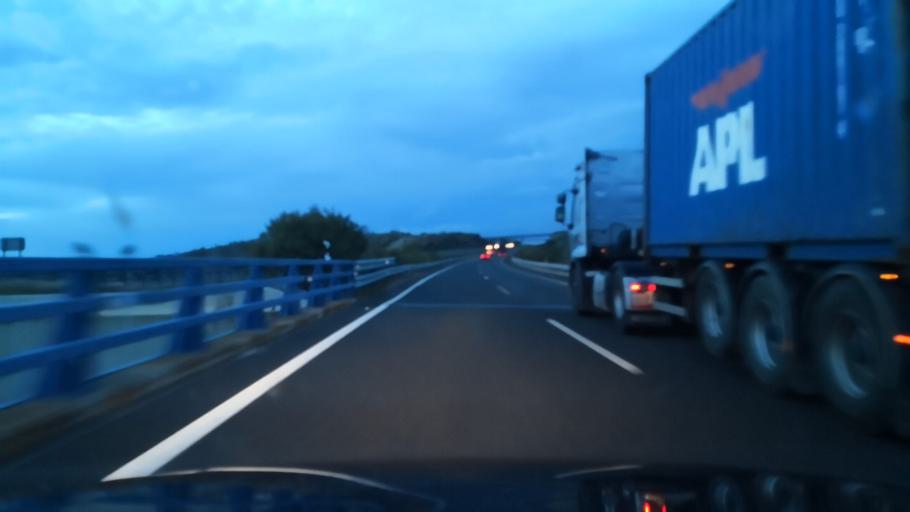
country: ES
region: Extremadura
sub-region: Provincia de Caceres
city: Hinojal
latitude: 39.6757
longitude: -6.3986
